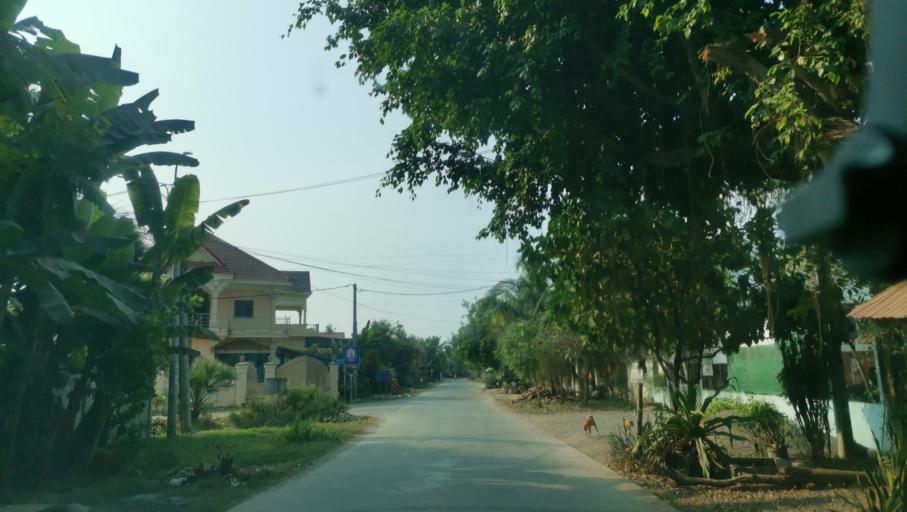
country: KH
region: Battambang
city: Battambang
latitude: 13.0876
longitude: 103.1934
